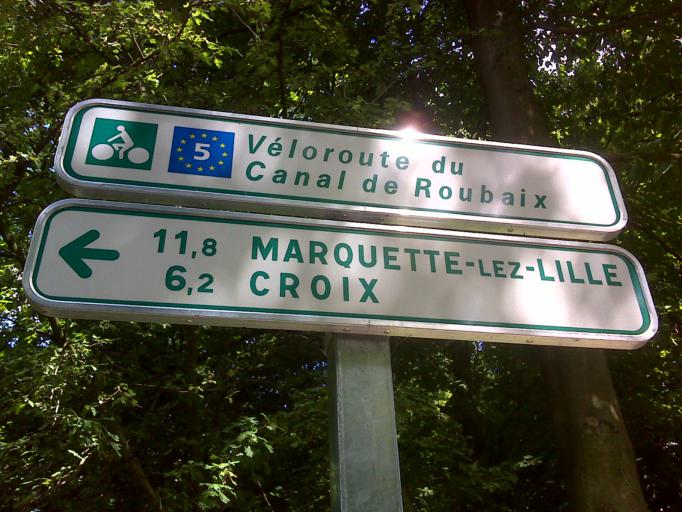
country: FR
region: Nord-Pas-de-Calais
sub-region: Departement du Nord
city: Roubaix
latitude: 50.7029
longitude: 3.1567
